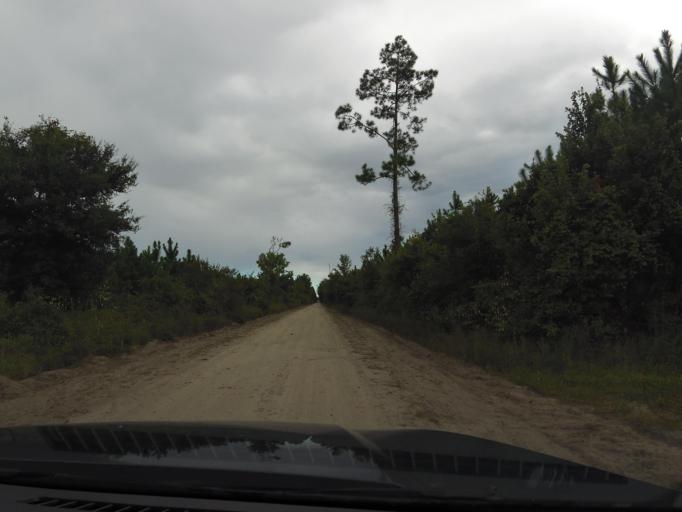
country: US
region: Florida
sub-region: Flagler County
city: Palm Coast
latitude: 29.5810
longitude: -81.3436
